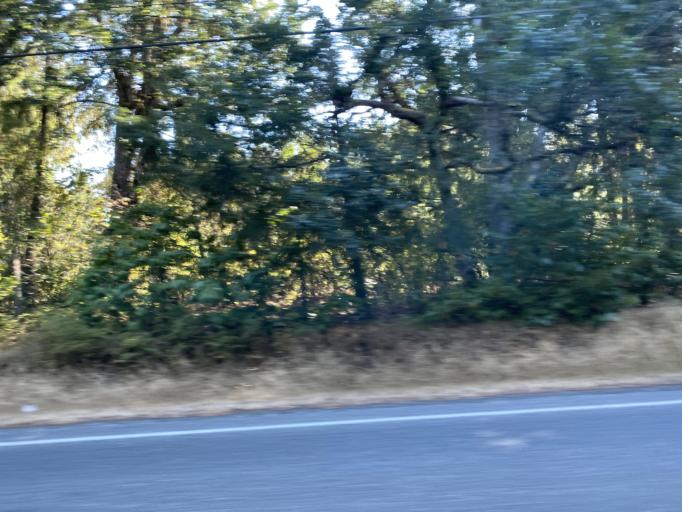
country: US
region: Washington
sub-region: Thurston County
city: Tanglewilde-Thompson Place
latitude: 47.0054
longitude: -122.7386
